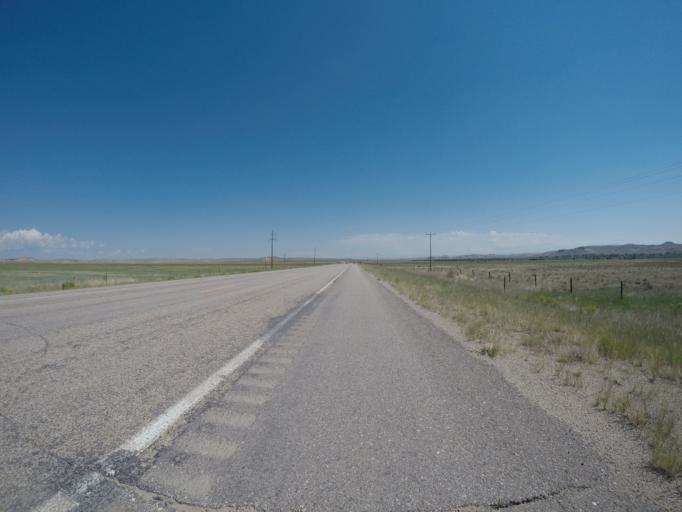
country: US
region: Wyoming
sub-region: Sublette County
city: Marbleton
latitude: 42.4130
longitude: -110.1163
